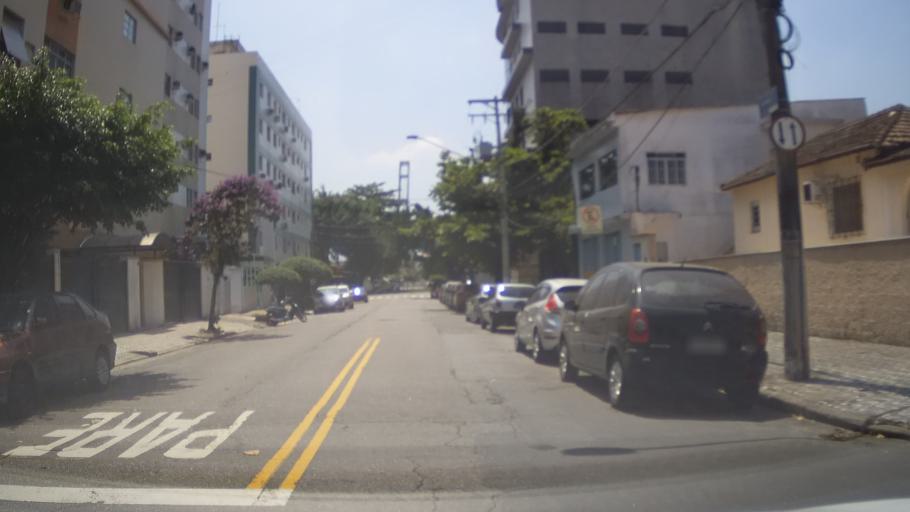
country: BR
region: Sao Paulo
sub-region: Santos
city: Santos
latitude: -23.9774
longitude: -46.2985
